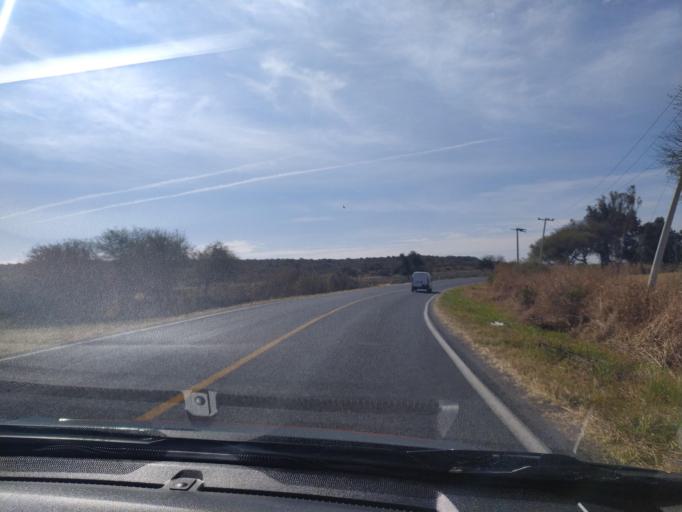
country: MX
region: Guanajuato
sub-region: San Francisco del Rincon
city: San Ignacio de Hidalgo
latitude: 20.9292
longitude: -101.8518
